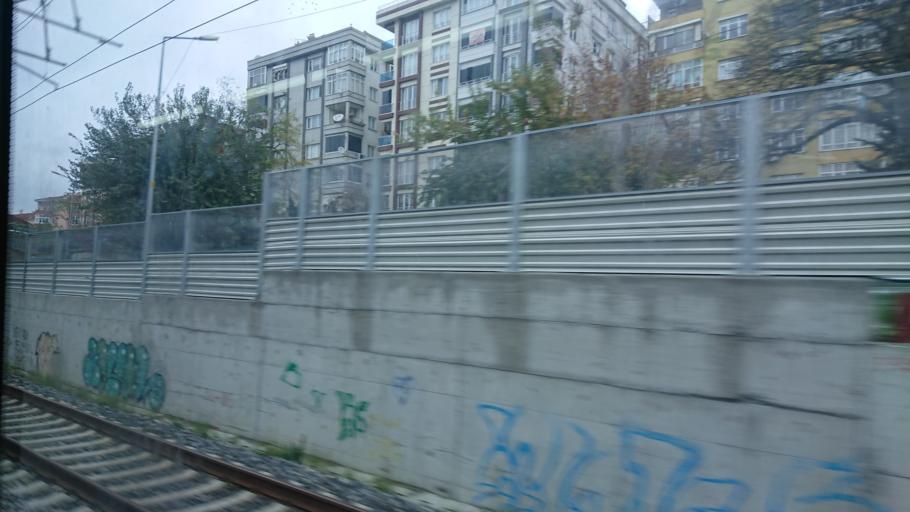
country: TR
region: Istanbul
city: Mahmutbey
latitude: 40.9932
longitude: 28.7700
